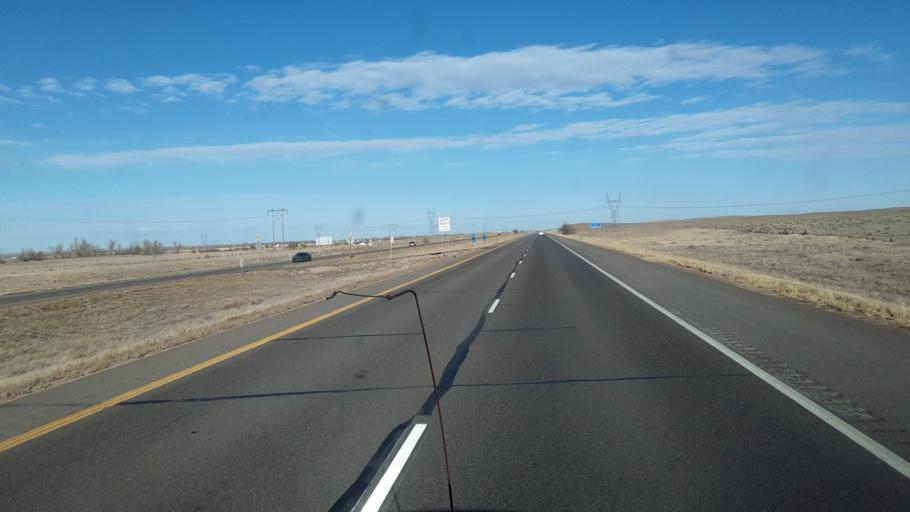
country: US
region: Colorado
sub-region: Morgan County
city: Brush
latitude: 40.2865
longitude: -103.5526
